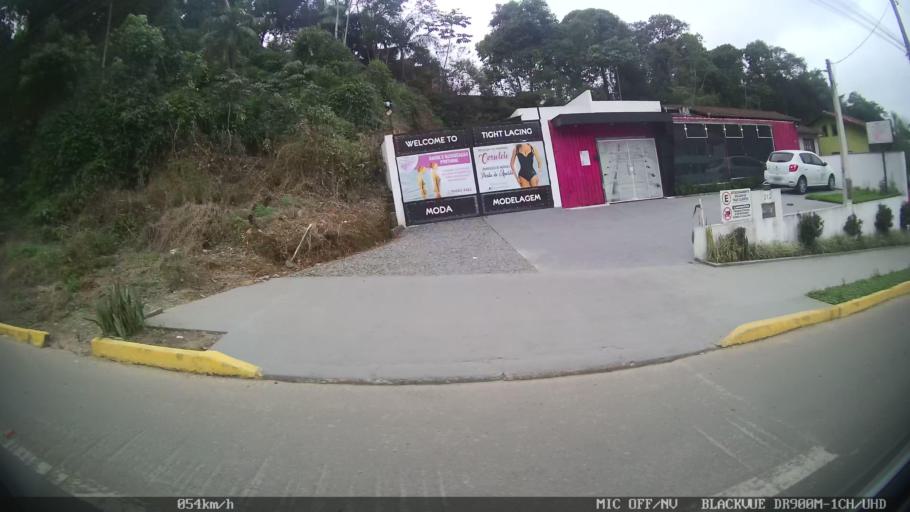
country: BR
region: Santa Catarina
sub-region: Joinville
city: Joinville
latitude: -26.3584
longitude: -48.8391
